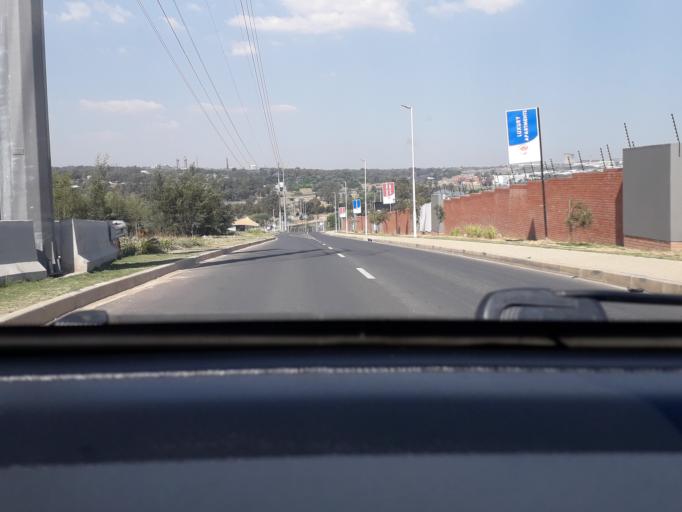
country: ZA
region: Gauteng
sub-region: City of Johannesburg Metropolitan Municipality
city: Modderfontein
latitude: -26.0945
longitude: 28.1394
